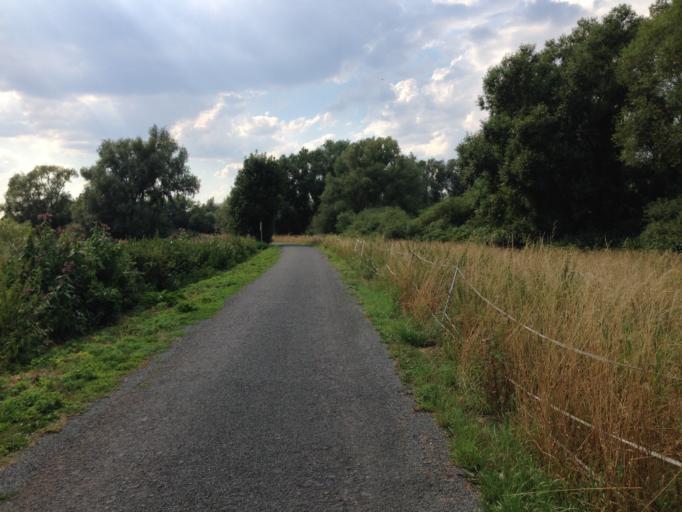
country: DE
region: Hesse
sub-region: Regierungsbezirk Giessen
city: Heuchelheim
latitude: 50.5708
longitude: 8.6337
